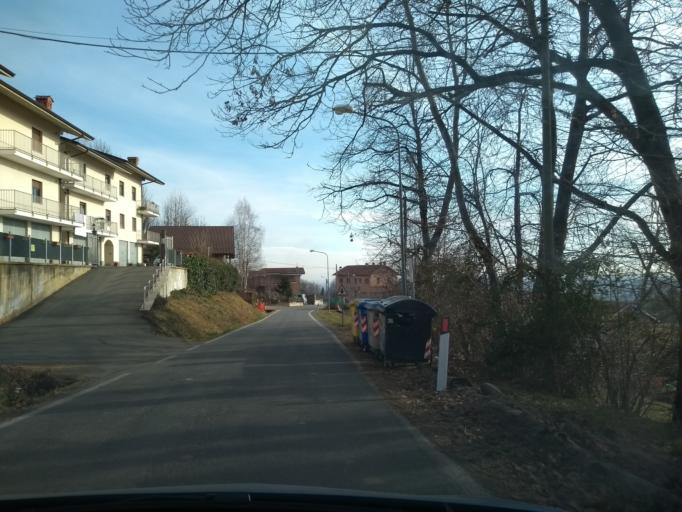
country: IT
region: Piedmont
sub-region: Provincia di Torino
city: Lanzo Torinese
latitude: 45.2950
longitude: 7.4904
